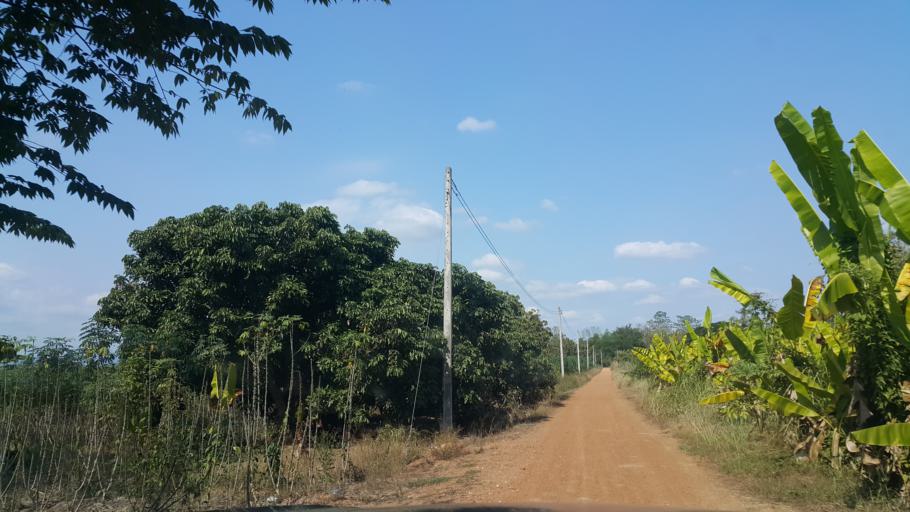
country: TH
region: Sukhothai
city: Thung Saliam
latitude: 17.3285
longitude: 99.5800
